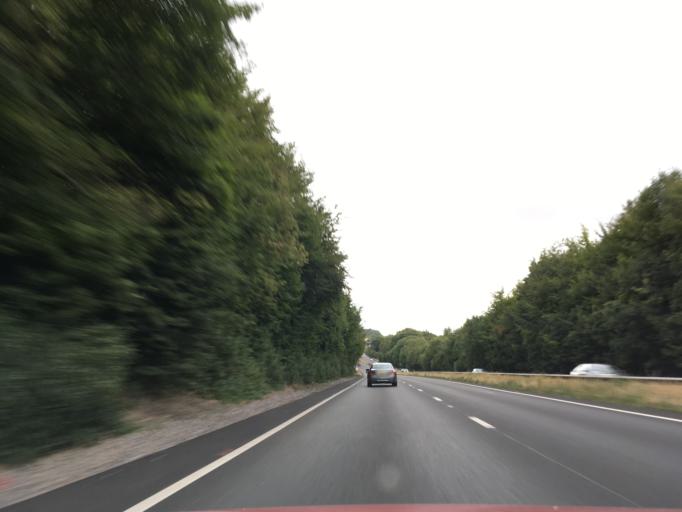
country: GB
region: England
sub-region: Hampshire
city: Kings Worthy
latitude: 51.1666
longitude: -1.3410
